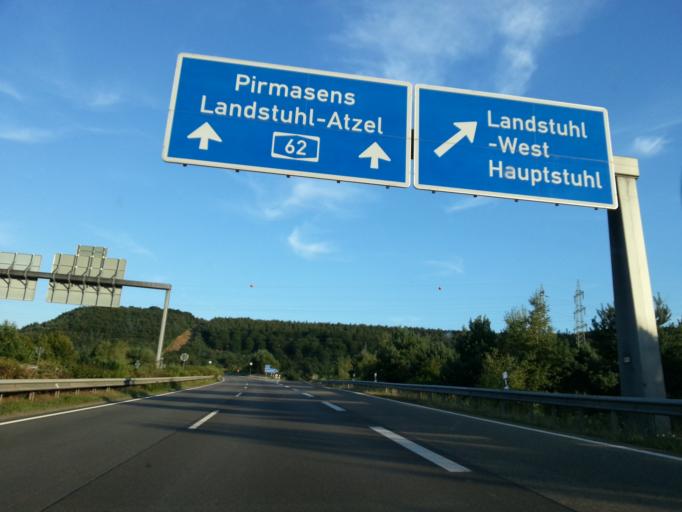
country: DE
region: Rheinland-Pfalz
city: Steinwenden
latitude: 49.4133
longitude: 7.5311
